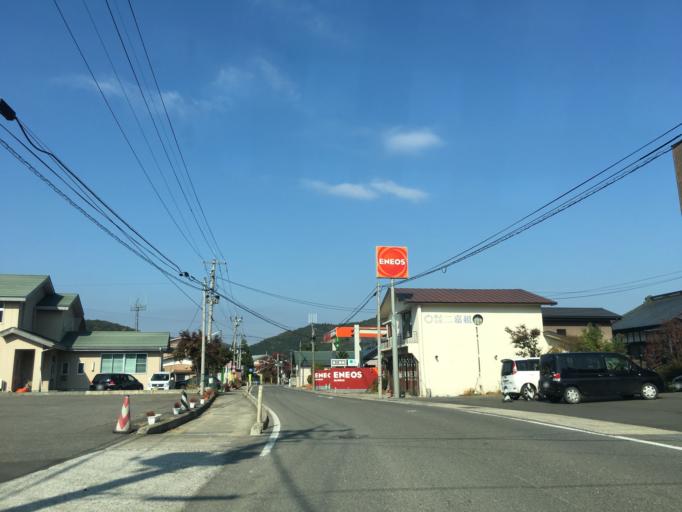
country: JP
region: Fukushima
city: Inawashiro
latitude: 37.3894
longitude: 140.0894
